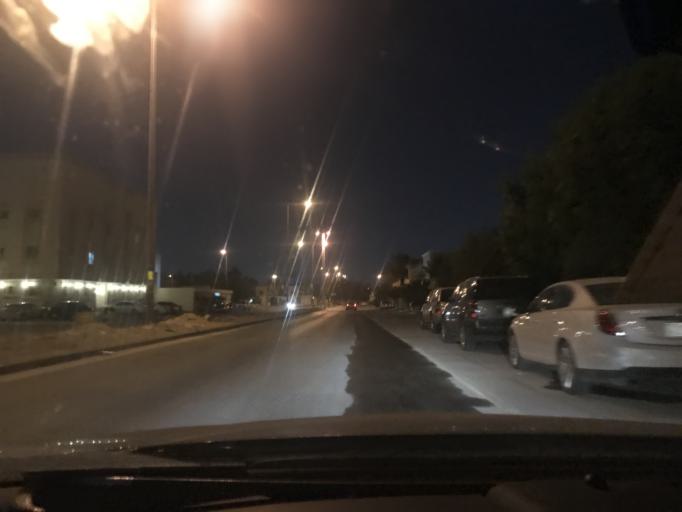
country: SA
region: Ar Riyad
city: Riyadh
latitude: 24.7594
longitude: 46.7444
